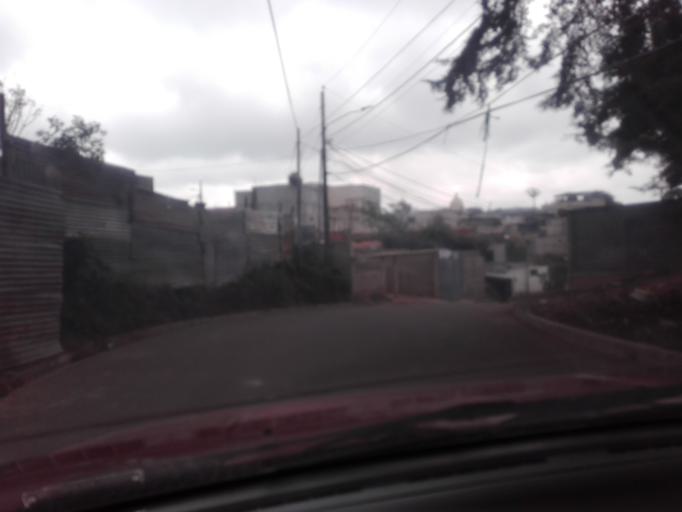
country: GT
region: Guatemala
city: San Jose Pinula
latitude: 14.5720
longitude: -90.4465
